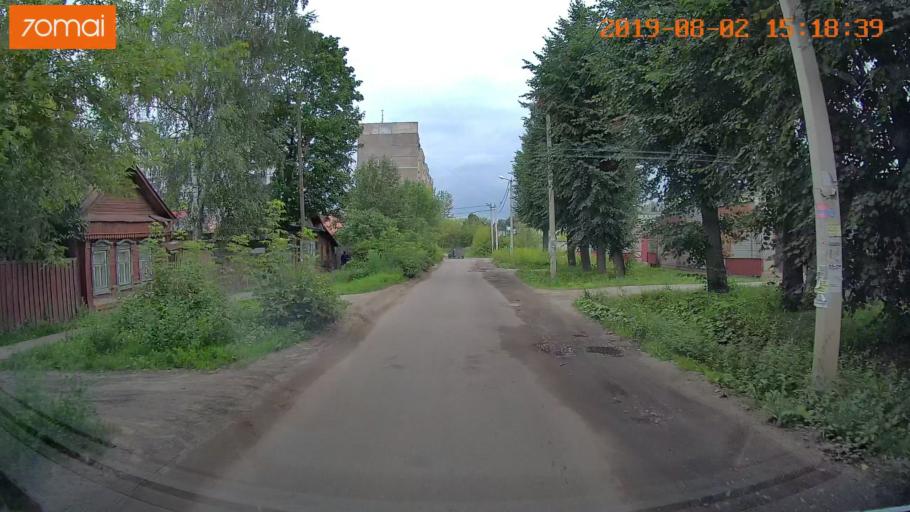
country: RU
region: Ivanovo
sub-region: Gorod Ivanovo
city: Ivanovo
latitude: 56.9800
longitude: 40.9717
